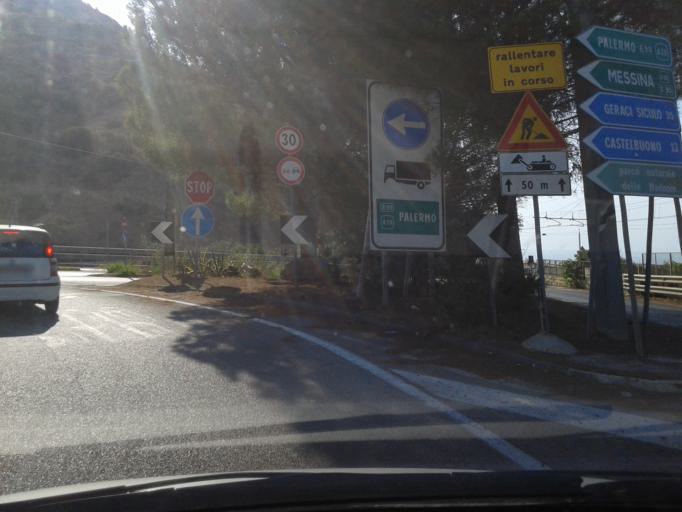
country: IT
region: Sicily
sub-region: Palermo
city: Pollina
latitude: 38.0150
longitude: 14.1044
